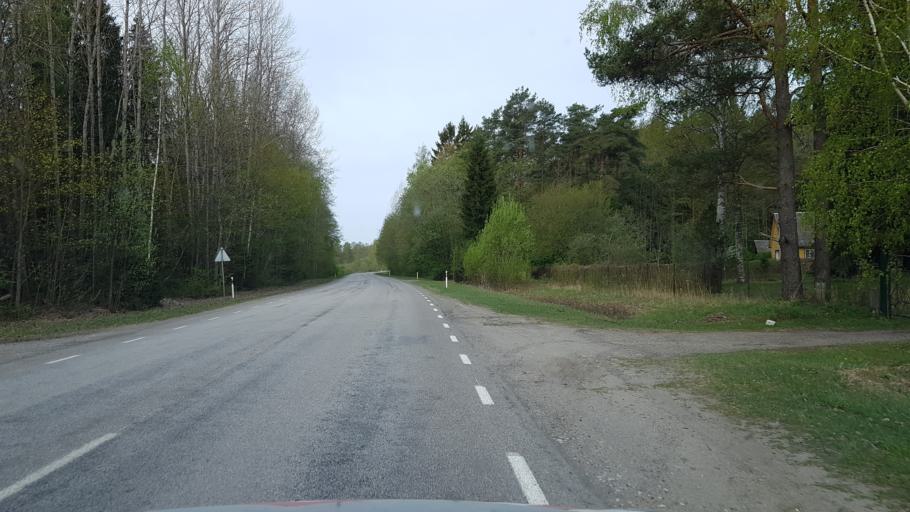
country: EE
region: Paernumaa
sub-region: Audru vald
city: Audru
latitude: 58.4072
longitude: 24.3216
